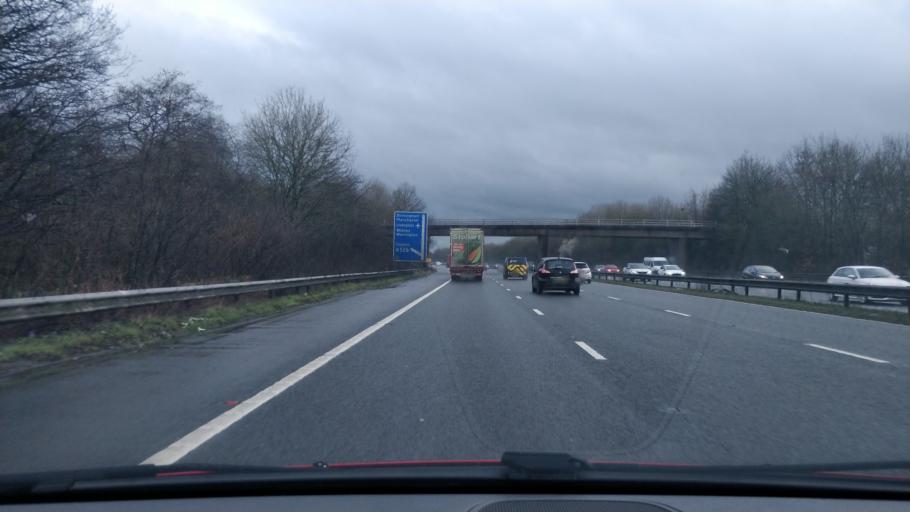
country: GB
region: England
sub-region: Knowsley
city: Knowsley
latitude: 53.4420
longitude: -2.8582
